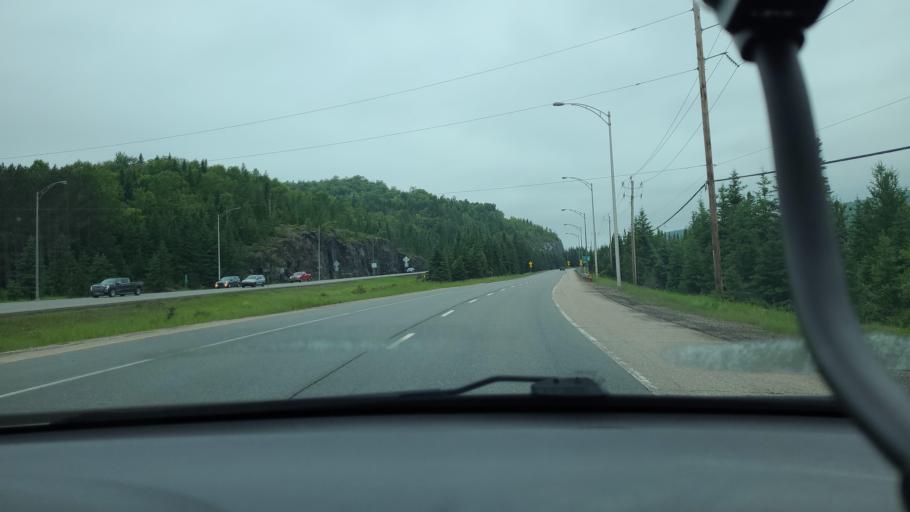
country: CA
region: Quebec
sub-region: Laurentides
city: Sainte-Agathe-des-Monts
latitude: 46.1045
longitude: -74.4147
